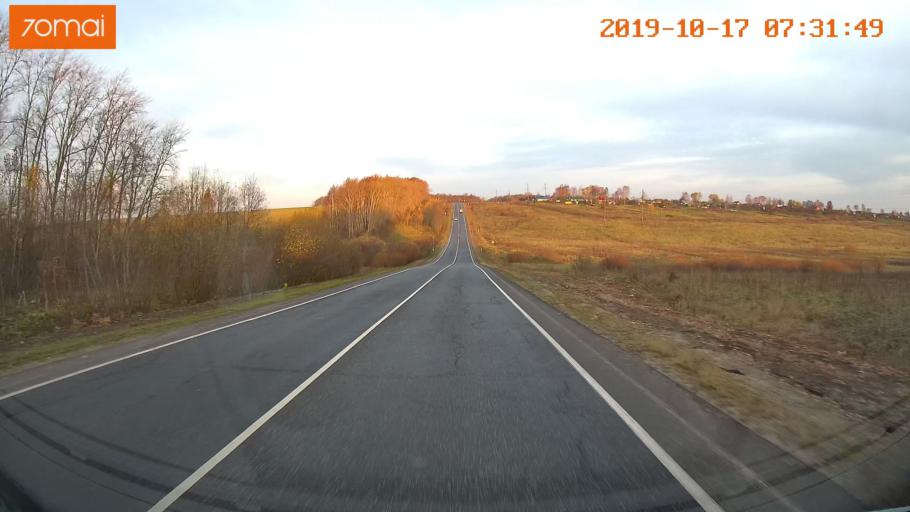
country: RU
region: Ivanovo
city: Gavrilov Posad
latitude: 56.3929
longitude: 39.9881
